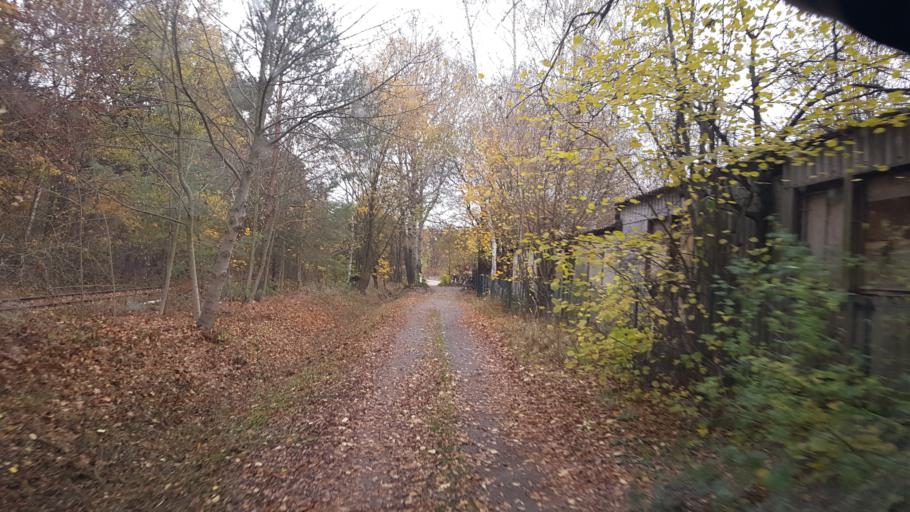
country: DE
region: Brandenburg
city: Crinitz
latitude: 51.7420
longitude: 13.7691
